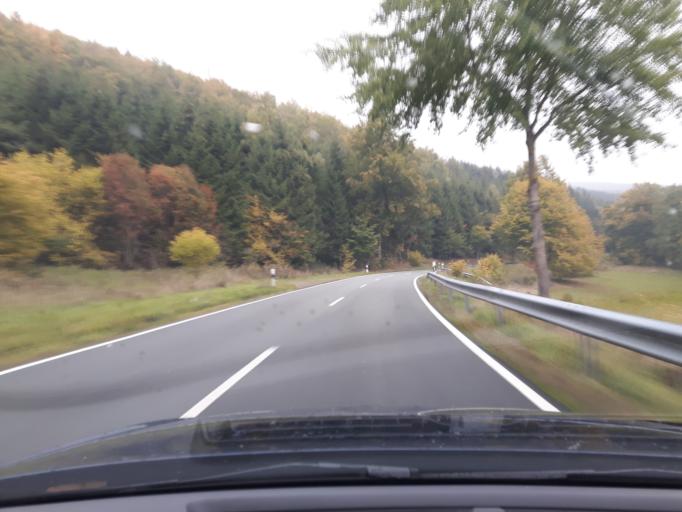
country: DE
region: North Rhine-Westphalia
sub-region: Regierungsbezirk Arnsberg
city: Bad Laasphe
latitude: 50.9604
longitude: 8.3891
